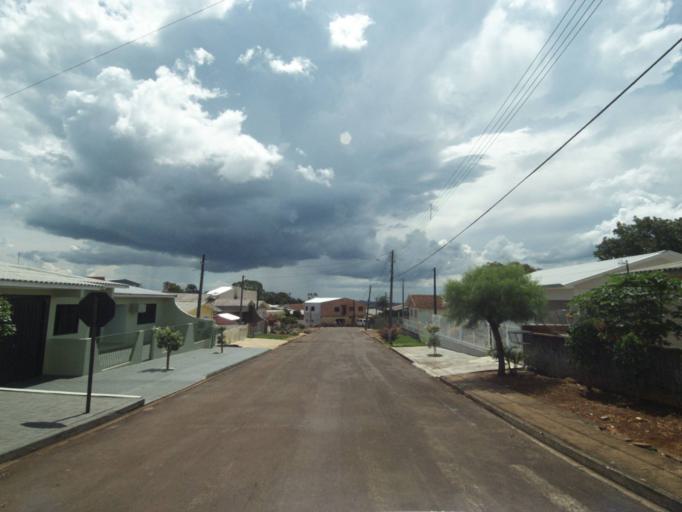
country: BR
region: Parana
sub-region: Guaraniacu
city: Guaraniacu
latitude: -25.0951
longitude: -52.8751
